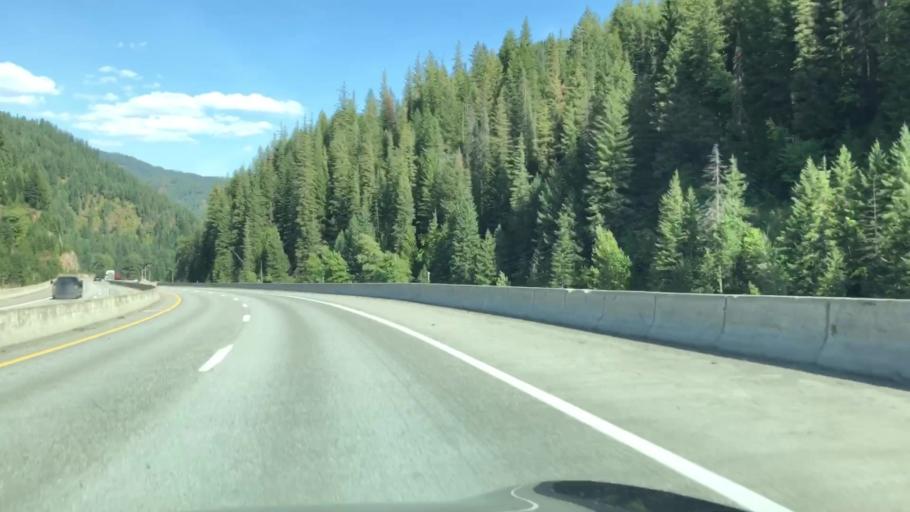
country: US
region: Idaho
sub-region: Shoshone County
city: Wallace
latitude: 47.4720
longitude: -115.9175
